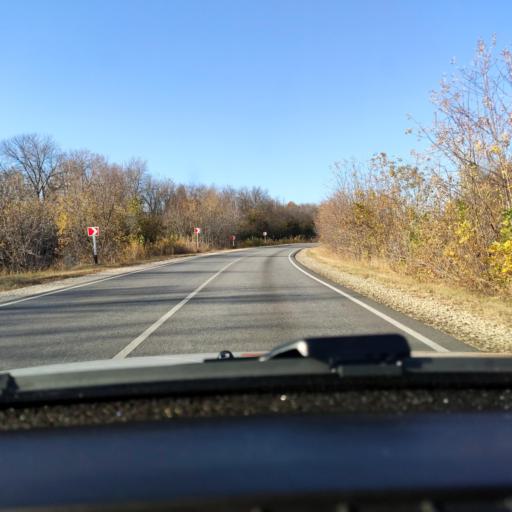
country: RU
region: Voronezj
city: Zemlyansk
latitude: 51.8501
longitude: 38.7972
